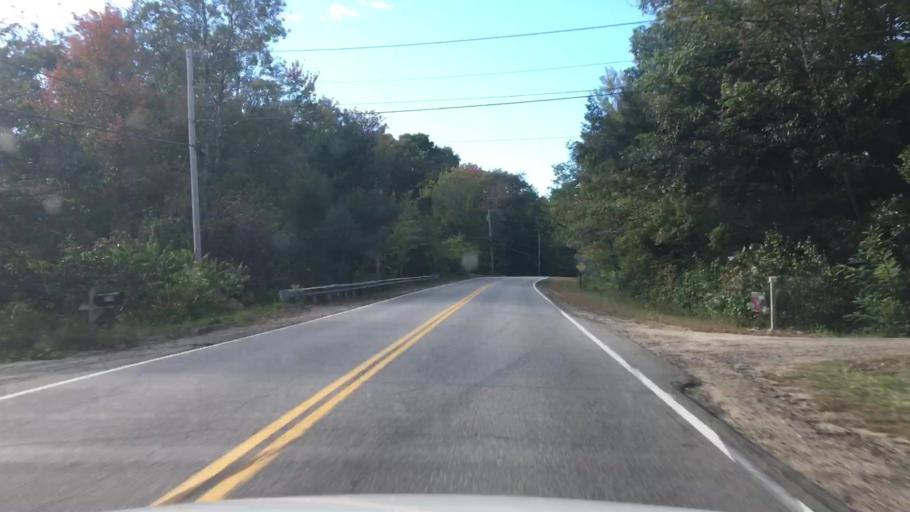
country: US
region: Maine
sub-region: Sagadahoc County
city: Topsham
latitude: 43.9350
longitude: -70.0167
